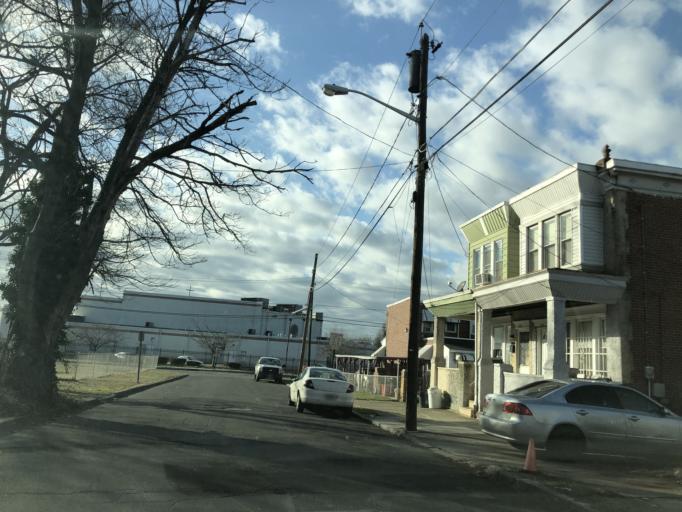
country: US
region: New Jersey
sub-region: Camden County
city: Camden
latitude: 39.9267
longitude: -75.1103
